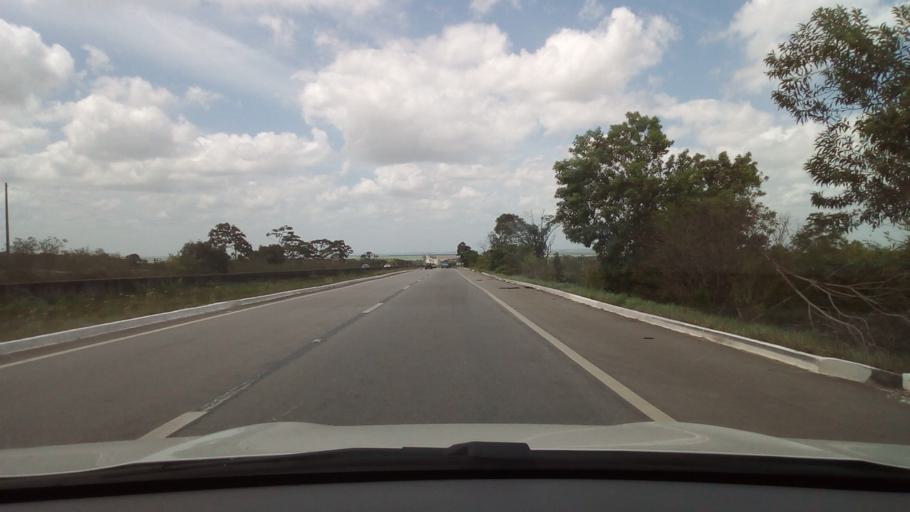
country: BR
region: Paraiba
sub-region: Mamanguape
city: Mamanguape
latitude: -6.9601
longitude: -35.0873
